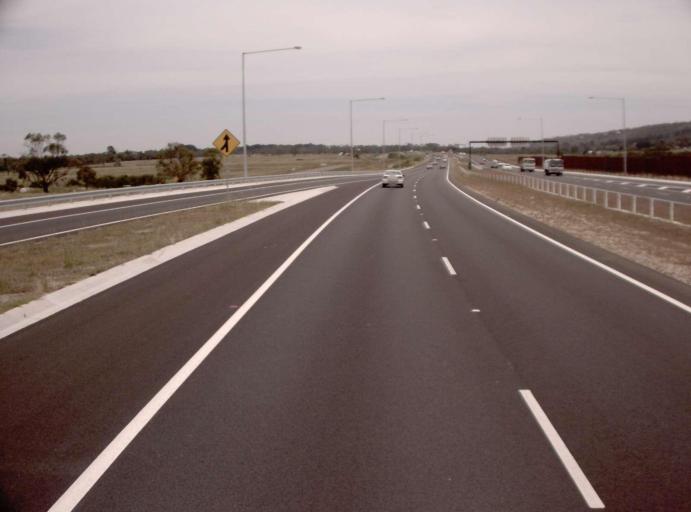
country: AU
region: Victoria
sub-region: Mornington Peninsula
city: Baxter
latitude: -38.1984
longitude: 145.1470
